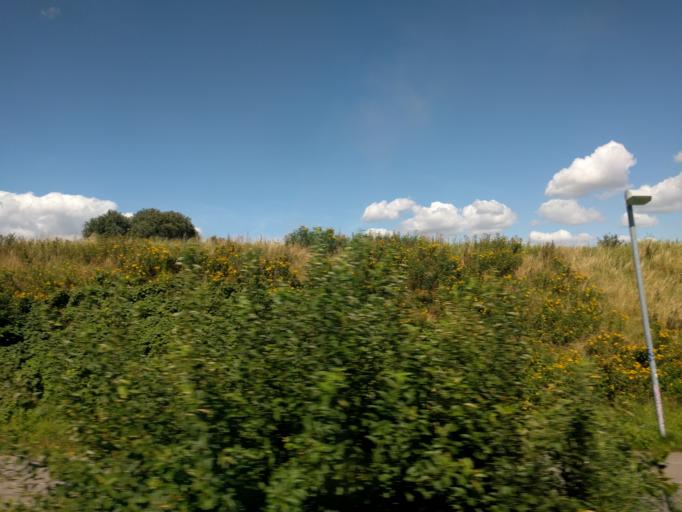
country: DK
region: Zealand
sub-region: Roskilde Kommune
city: Vindinge
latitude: 55.6476
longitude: 12.1257
